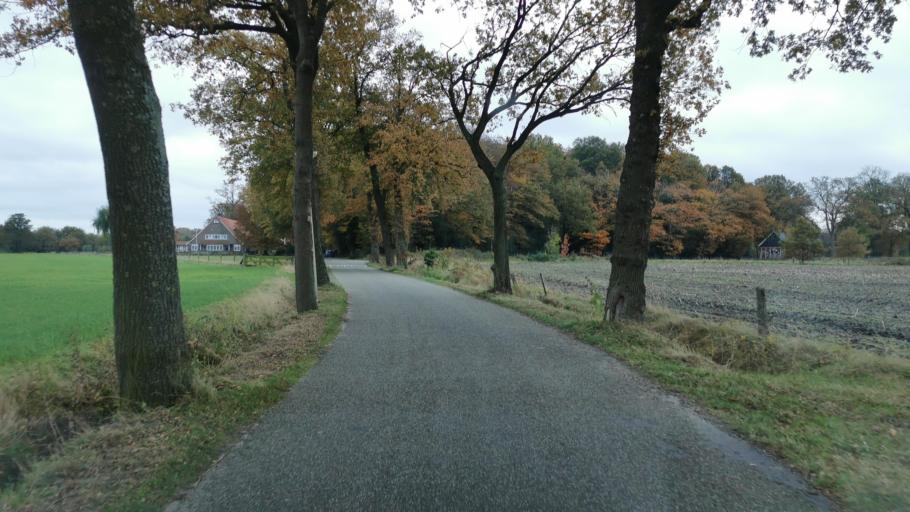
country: NL
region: Overijssel
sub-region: Gemeente Enschede
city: Enschede
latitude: 52.2085
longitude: 6.9198
